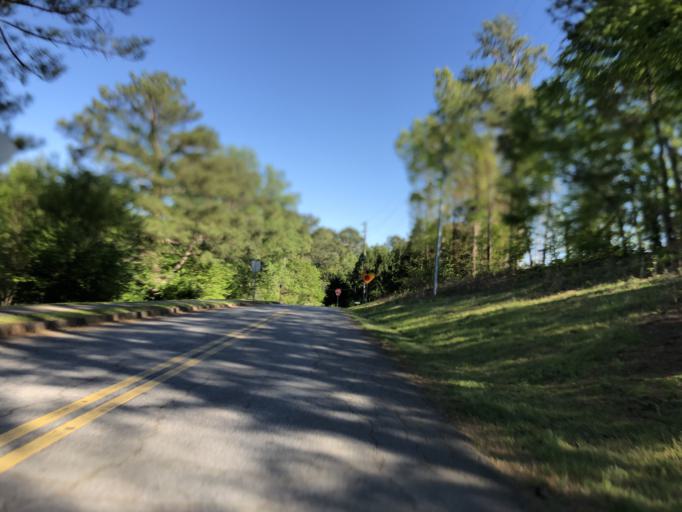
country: US
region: Georgia
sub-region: DeKalb County
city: North Druid Hills
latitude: 33.8066
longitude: -84.3061
